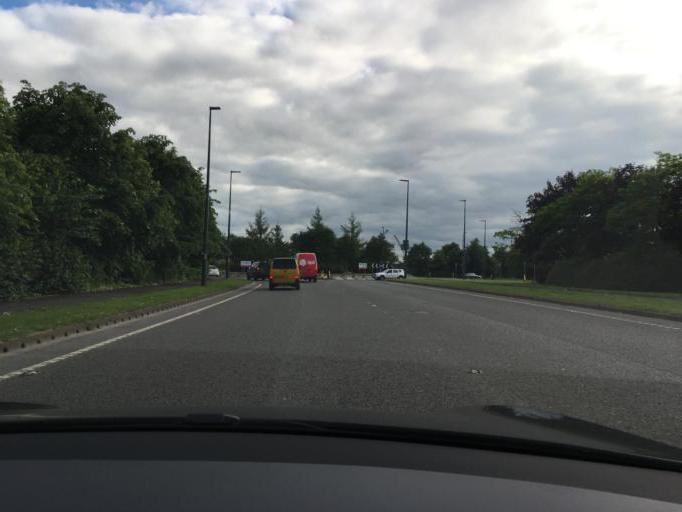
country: GB
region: England
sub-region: City and Borough of Salford
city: Irlam
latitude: 53.4310
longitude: -2.4241
